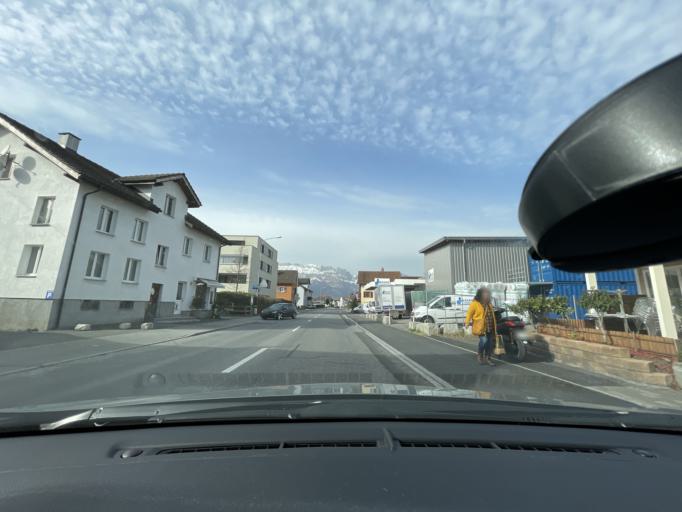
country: CH
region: Saint Gallen
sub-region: Wahlkreis Werdenberg
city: Buchs
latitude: 47.1492
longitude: 9.4833
